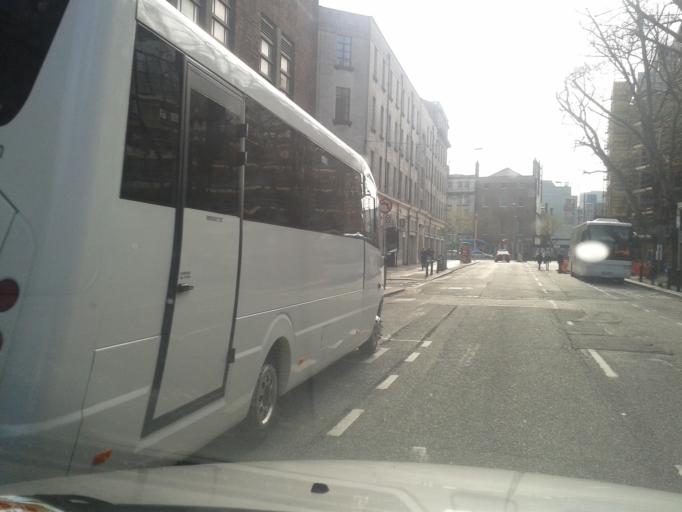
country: IE
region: Leinster
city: Drumcondra
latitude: 53.3524
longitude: -6.2595
